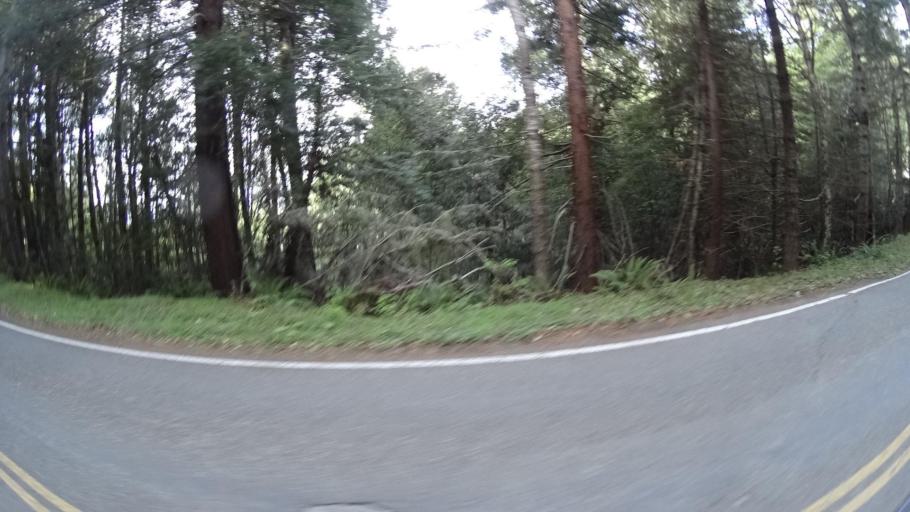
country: US
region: California
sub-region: Humboldt County
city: Bayside
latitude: 40.7515
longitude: -123.9834
